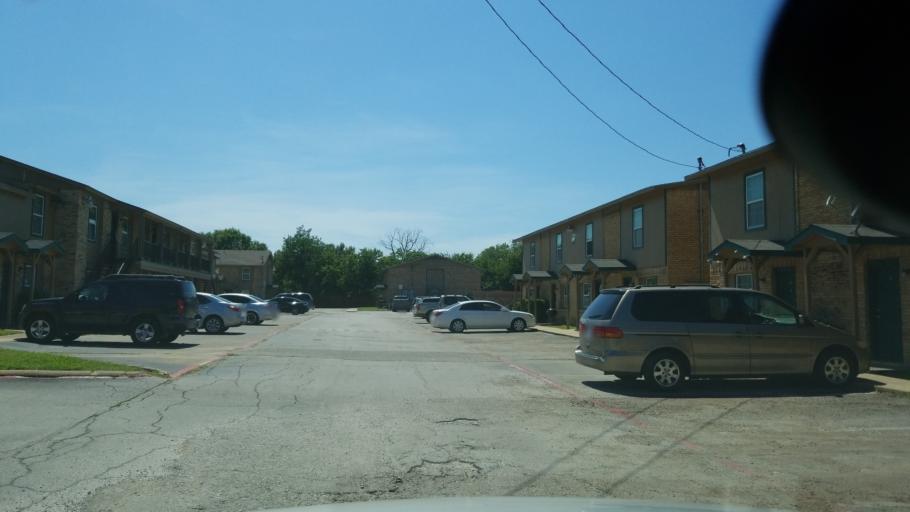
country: US
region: Texas
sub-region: Dallas County
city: Irving
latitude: 32.8303
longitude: -96.9361
